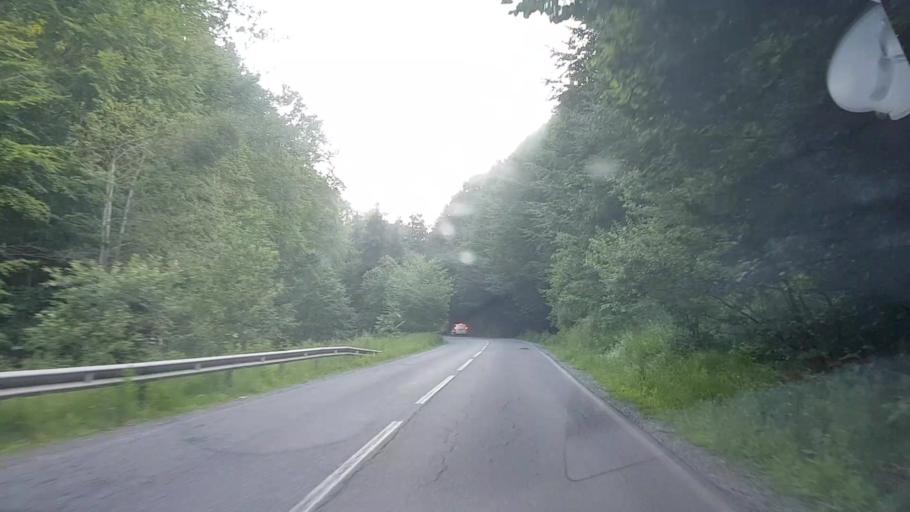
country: RO
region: Harghita
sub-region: Comuna Praid
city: Ocna de Sus
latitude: 46.5799
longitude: 25.2340
